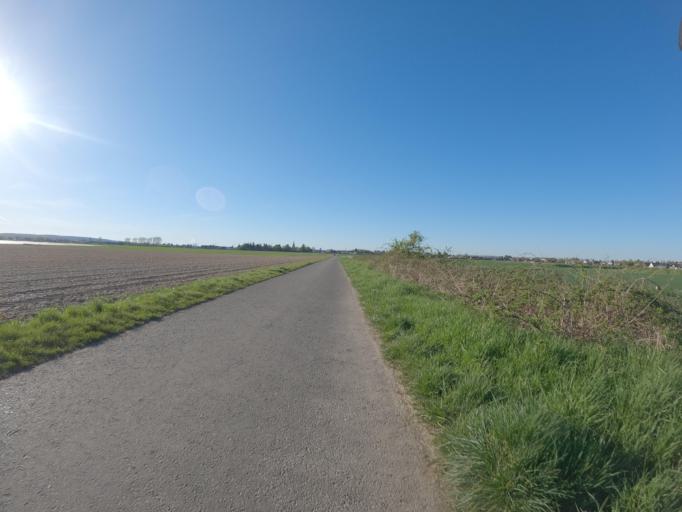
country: DE
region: North Rhine-Westphalia
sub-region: Regierungsbezirk Koln
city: Dueren
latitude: 50.7860
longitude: 6.4563
